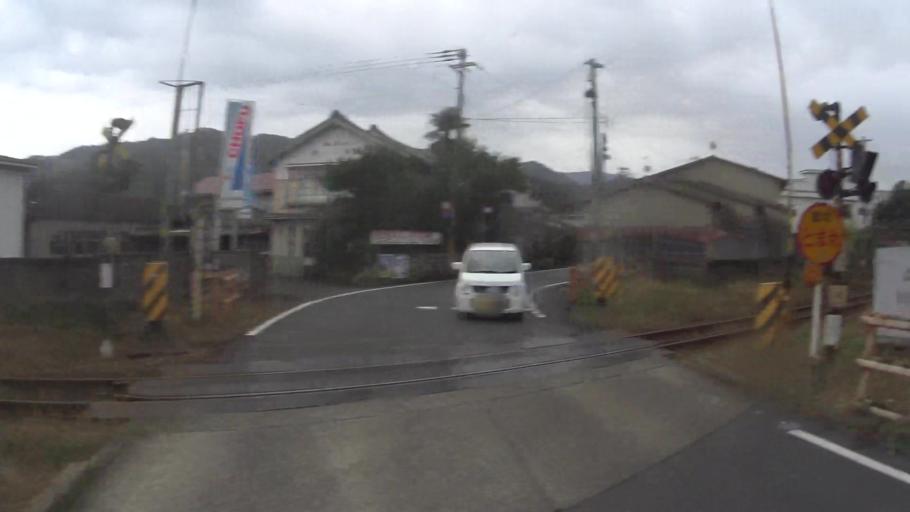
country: JP
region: Kyoto
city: Miyazu
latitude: 35.5361
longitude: 135.2020
